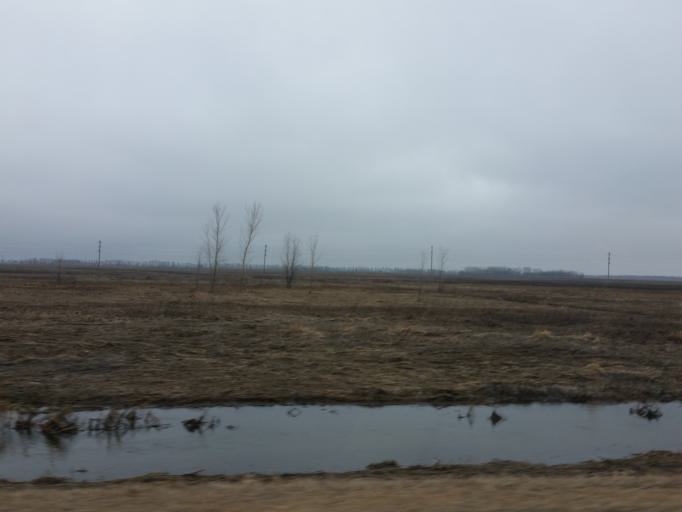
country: US
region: North Dakota
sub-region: Walsh County
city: Grafton
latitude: 48.3532
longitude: -97.1851
